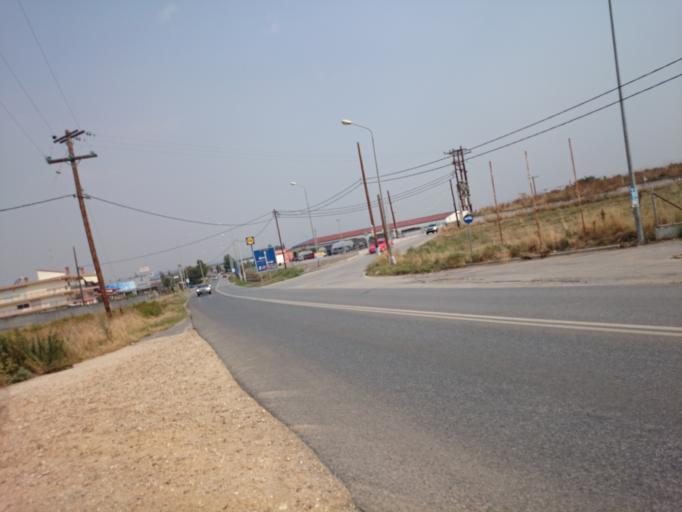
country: GR
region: Central Macedonia
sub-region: Nomos Chalkidikis
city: Nea Moudhania
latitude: 40.2576
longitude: 23.2755
